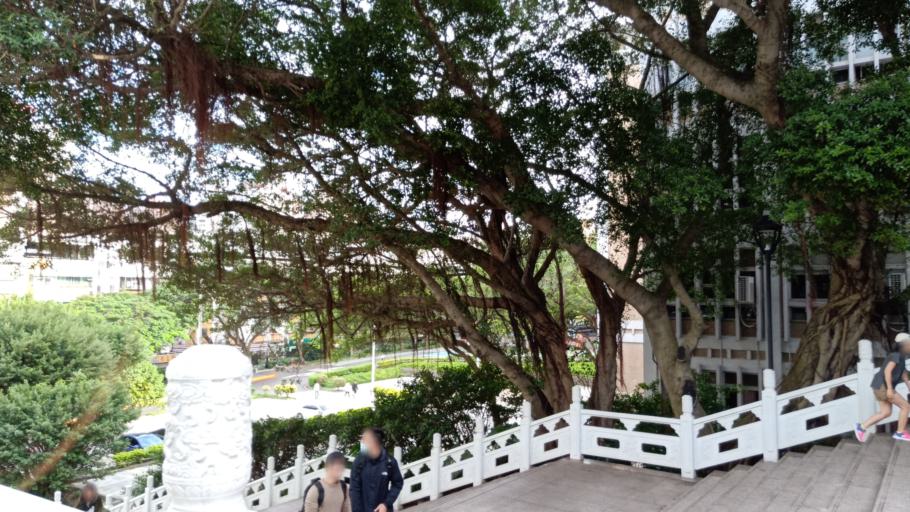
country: TW
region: Taipei
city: Taipei
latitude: 25.1762
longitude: 121.4489
